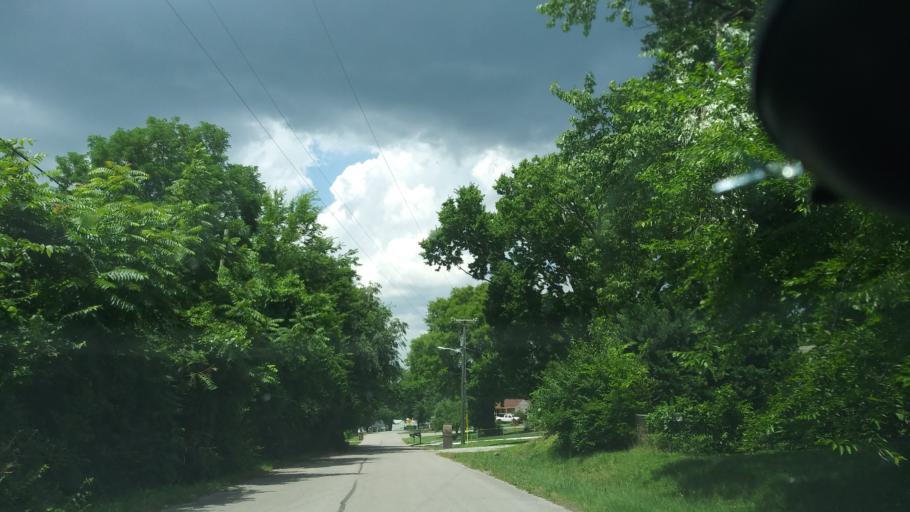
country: US
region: Tennessee
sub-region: Davidson County
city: Oak Hill
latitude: 36.1252
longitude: -86.7611
